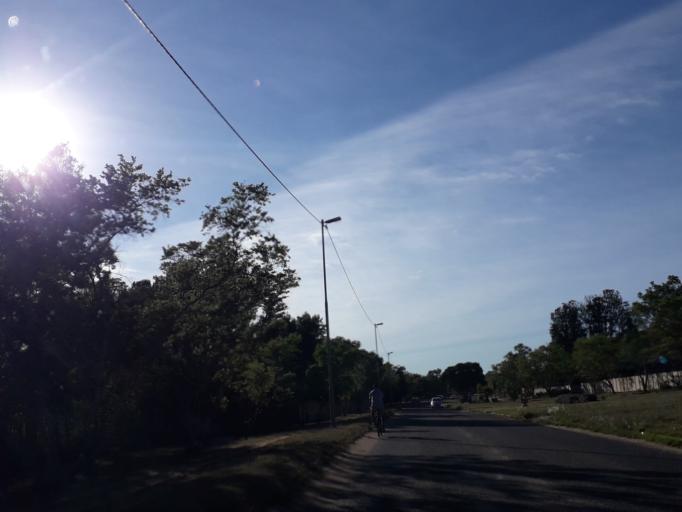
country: ZA
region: Gauteng
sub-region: City of Johannesburg Metropolitan Municipality
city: Roodepoort
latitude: -26.0909
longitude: 27.8984
